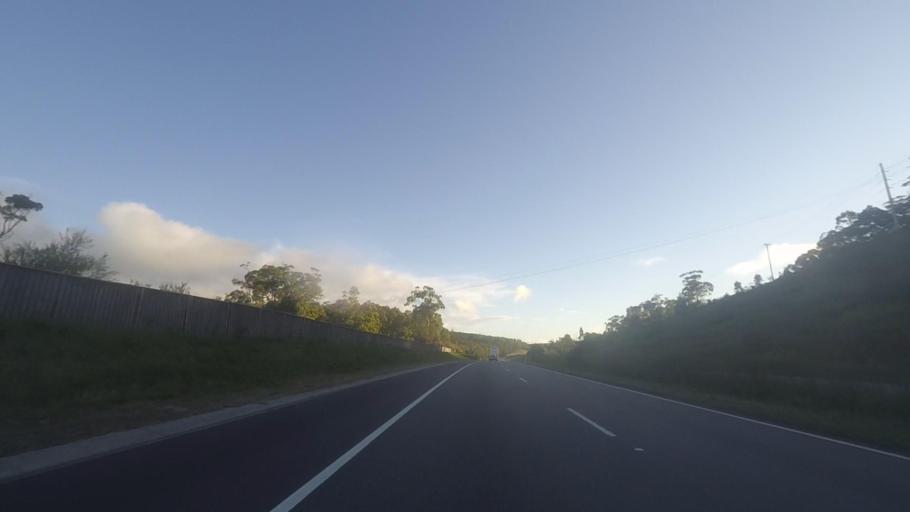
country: AU
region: New South Wales
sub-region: Great Lakes
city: Bulahdelah
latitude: -32.5072
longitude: 152.2113
